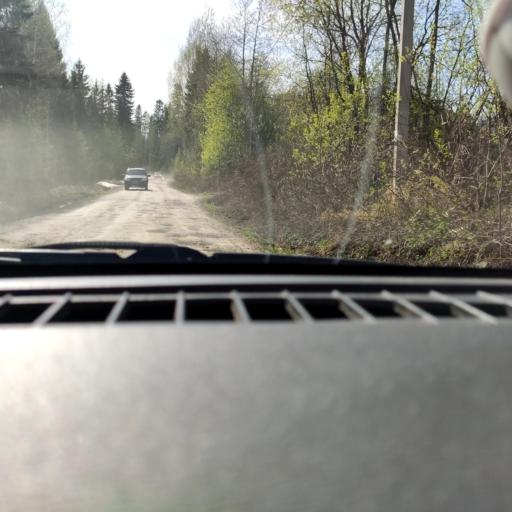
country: RU
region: Perm
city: Kondratovo
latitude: 58.2579
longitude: 56.1035
